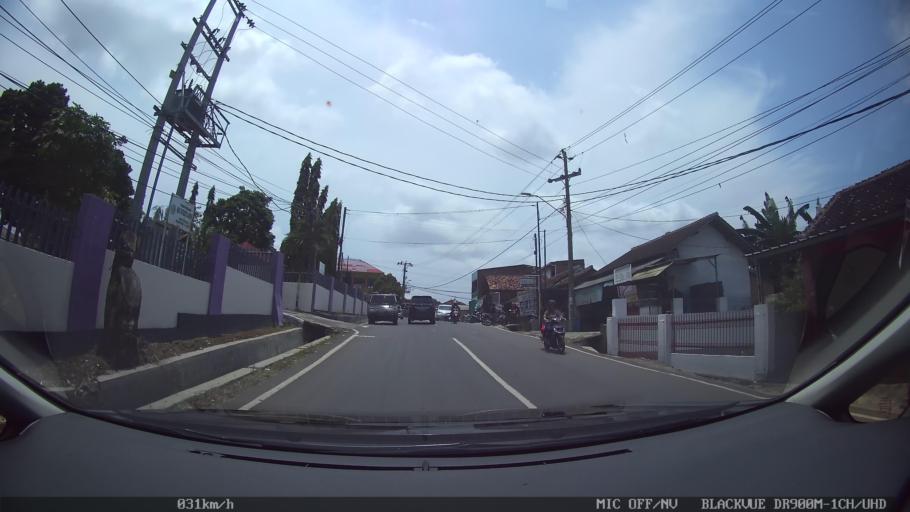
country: ID
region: Lampung
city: Kedaton
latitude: -5.3935
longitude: 105.2488
